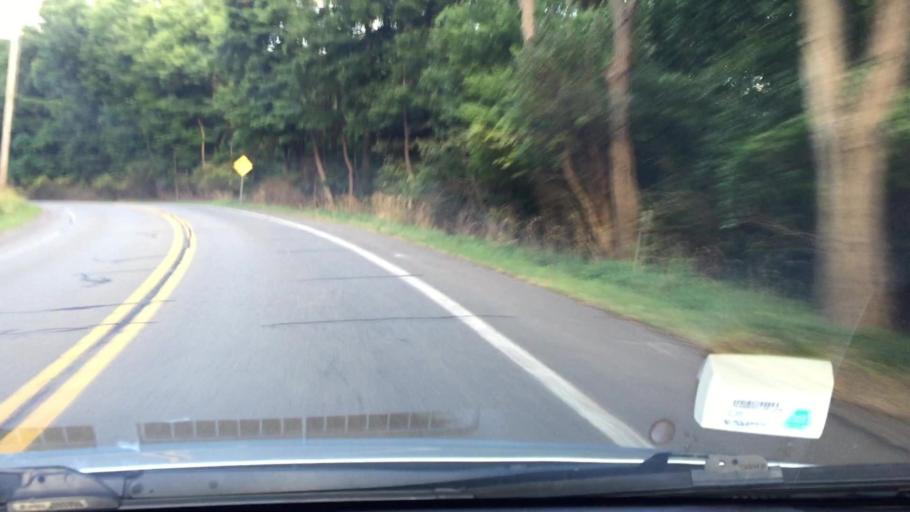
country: US
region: Pennsylvania
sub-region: Allegheny County
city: Gibsonia
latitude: 40.6307
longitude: -79.9784
